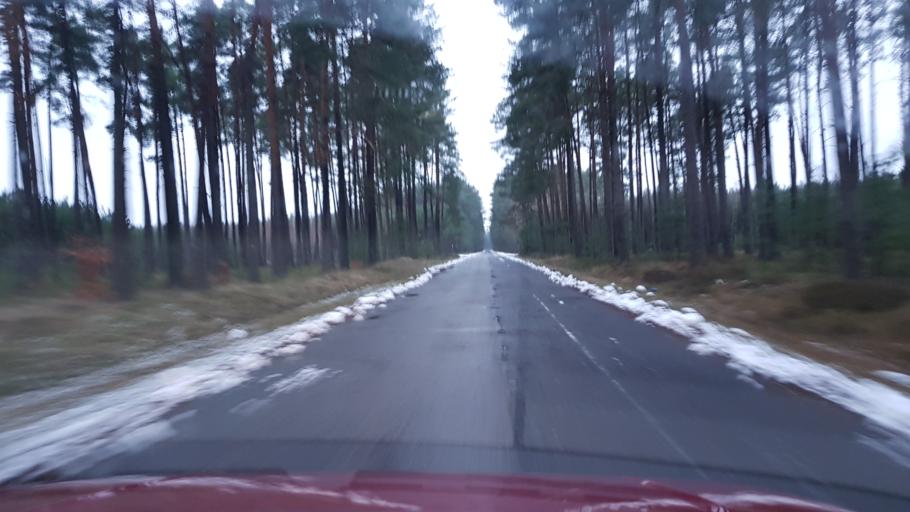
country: PL
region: West Pomeranian Voivodeship
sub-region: Powiat goleniowski
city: Goleniow
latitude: 53.4811
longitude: 14.8451
